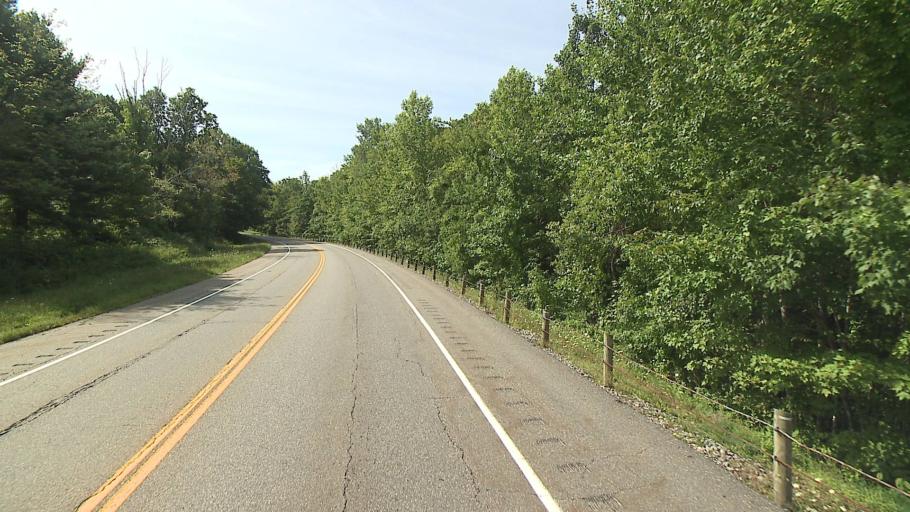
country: US
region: Connecticut
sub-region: Litchfield County
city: Litchfield
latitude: 41.7586
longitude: -73.1581
